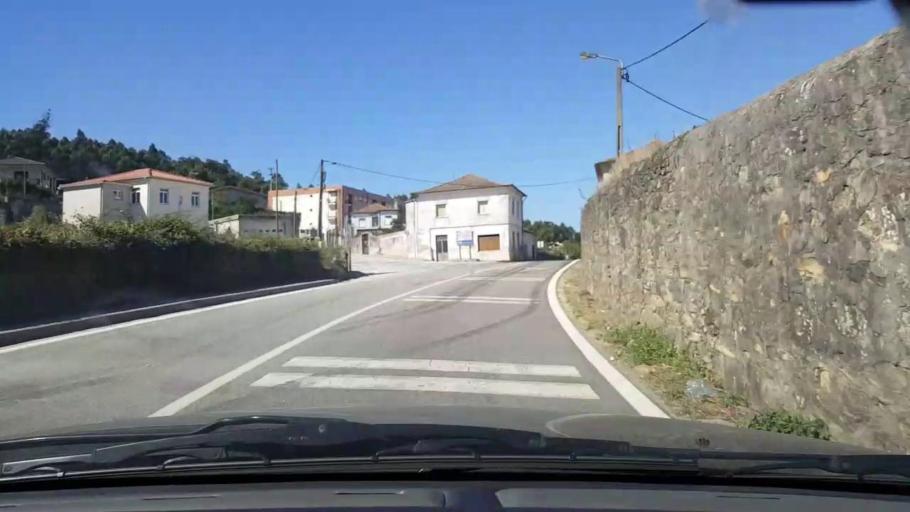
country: PT
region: Porto
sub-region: Maia
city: Gemunde
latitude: 41.3383
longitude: -8.6446
